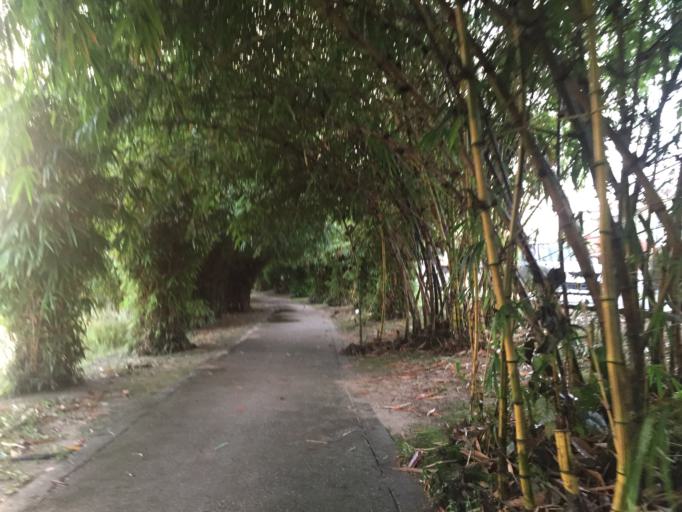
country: MY
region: Selangor
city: Klang
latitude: 2.9884
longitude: 101.4363
